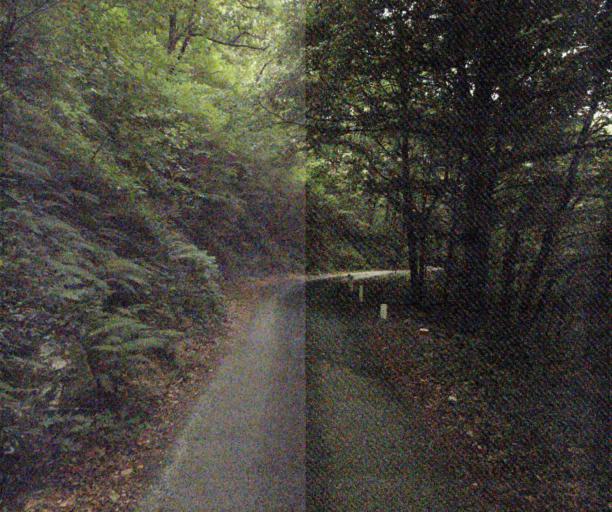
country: FR
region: Midi-Pyrenees
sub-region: Departement du Tarn
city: Soreze
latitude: 43.4254
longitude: 2.0795
